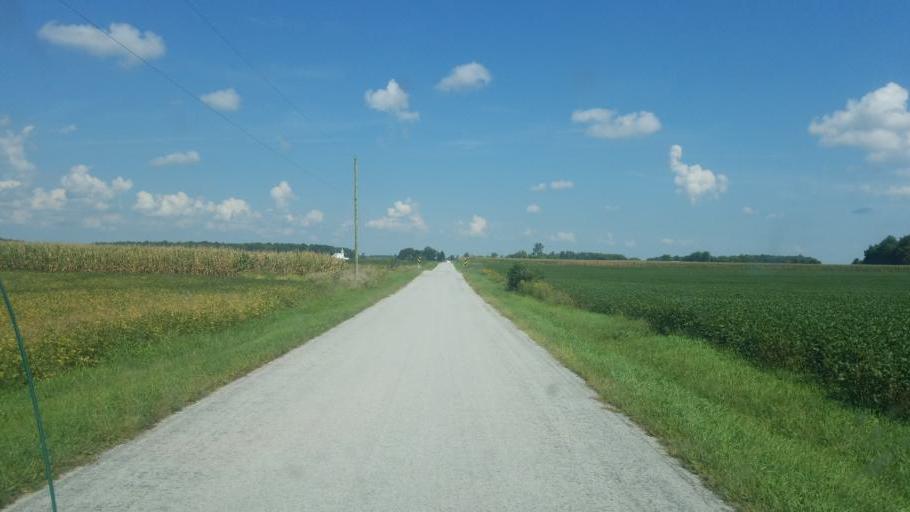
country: US
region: Ohio
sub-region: Hardin County
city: Kenton
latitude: 40.6790
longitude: -83.4957
